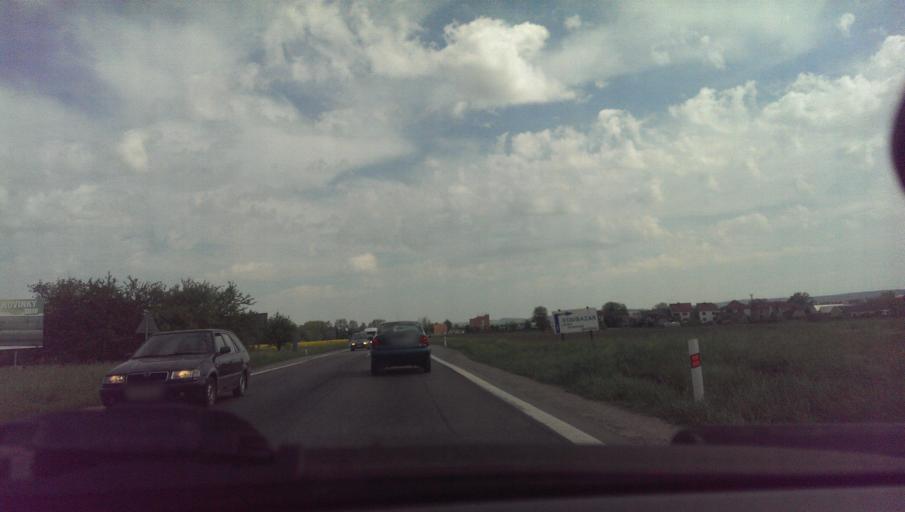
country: CZ
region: Zlin
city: Babice
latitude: 49.1244
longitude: 17.4771
